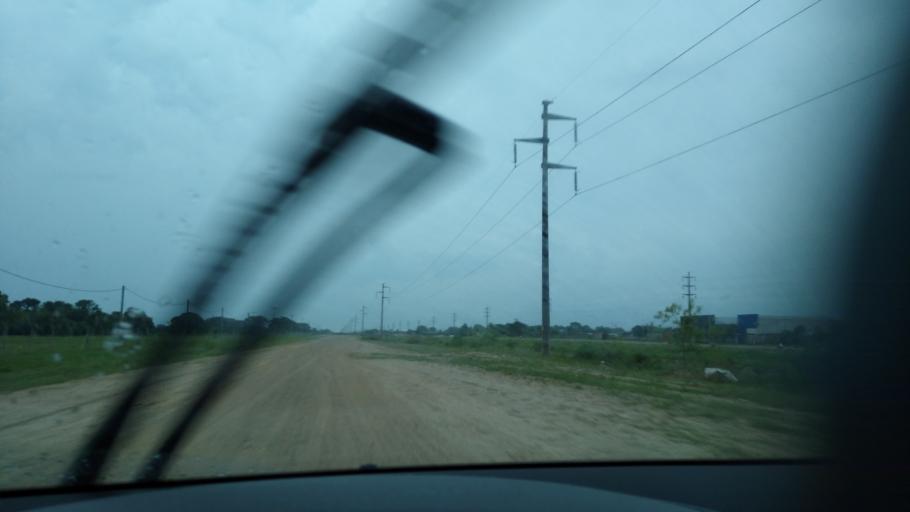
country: AR
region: Chaco
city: Puerto Vilelas
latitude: -27.5014
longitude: -58.9743
